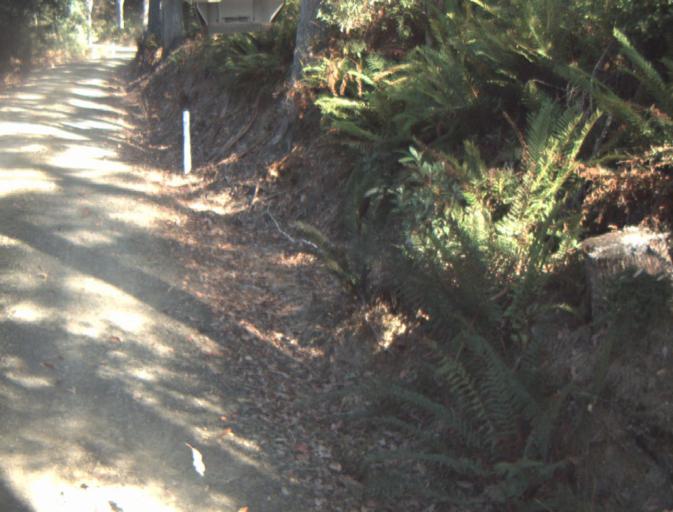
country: AU
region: Tasmania
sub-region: Dorset
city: Scottsdale
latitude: -41.2738
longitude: 147.3688
